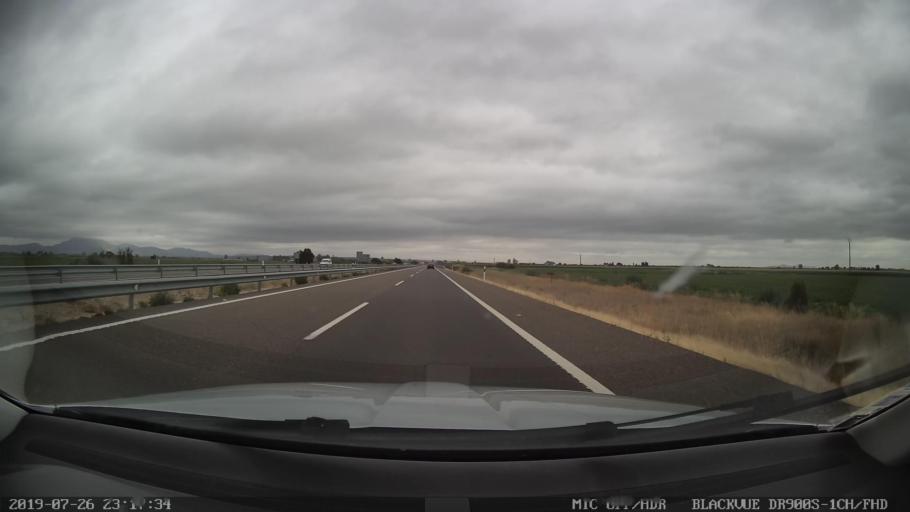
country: ES
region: Extremadura
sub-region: Provincia de Badajoz
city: Santa Amalia
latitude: 39.0826
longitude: -6.0251
